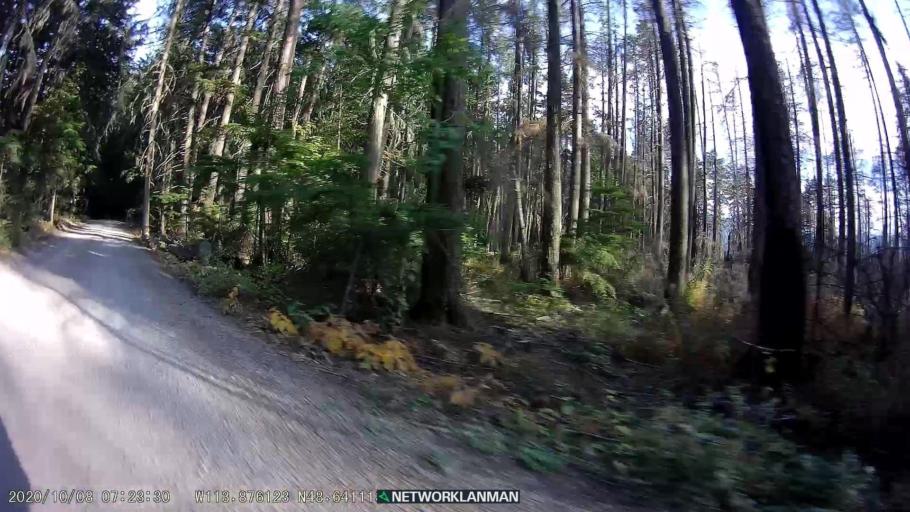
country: US
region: Montana
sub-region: Flathead County
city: Columbia Falls
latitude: 48.6411
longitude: -113.8759
